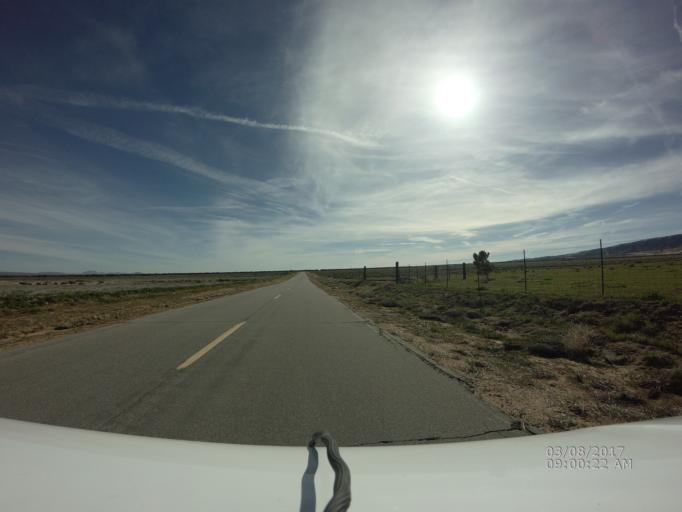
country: US
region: California
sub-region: Los Angeles County
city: Green Valley
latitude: 34.7610
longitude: -118.5215
